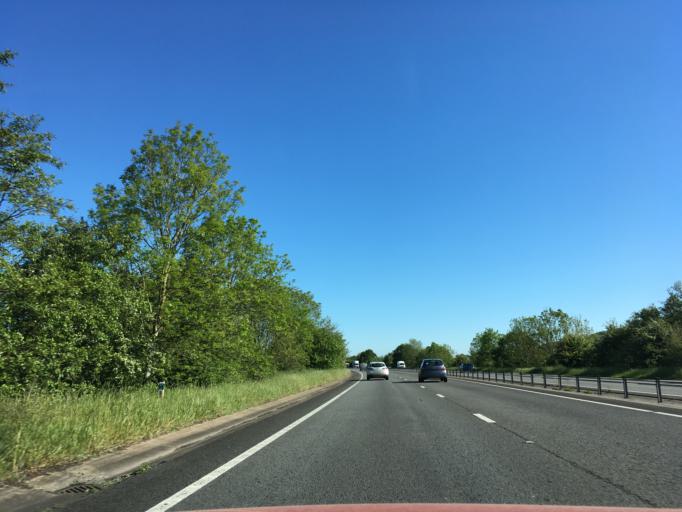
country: GB
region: Wales
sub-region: Monmouthshire
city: Llangwm
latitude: 51.7362
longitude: -2.8416
